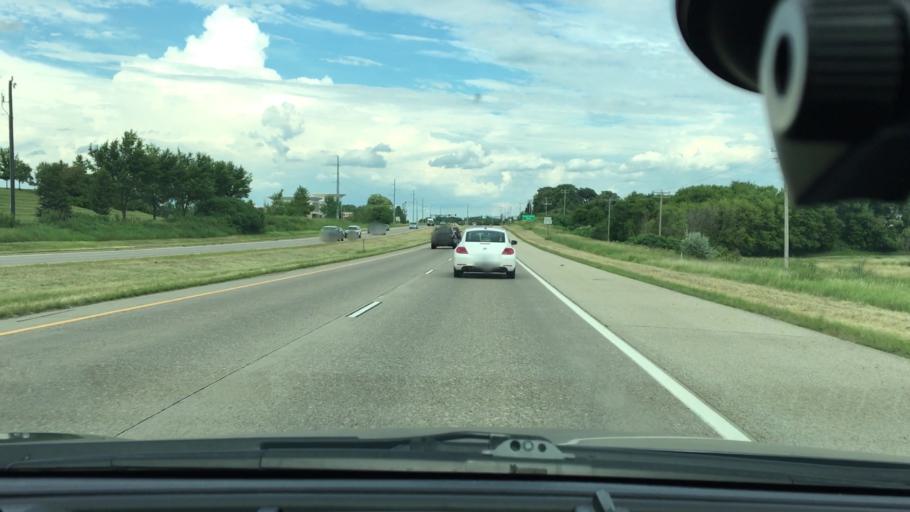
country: US
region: Minnesota
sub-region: Hennepin County
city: Shorewood
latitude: 44.8631
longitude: -93.5862
